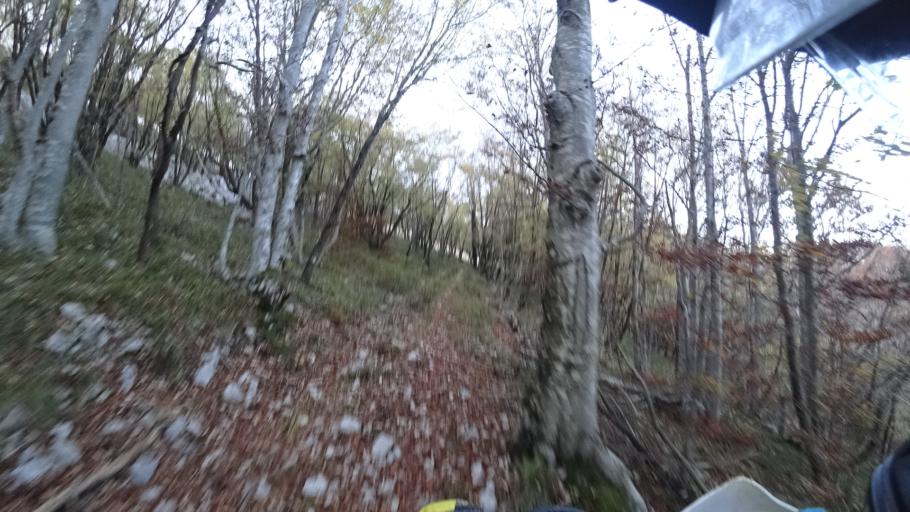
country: HR
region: Primorsko-Goranska
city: Klana
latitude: 45.5017
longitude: 14.4140
